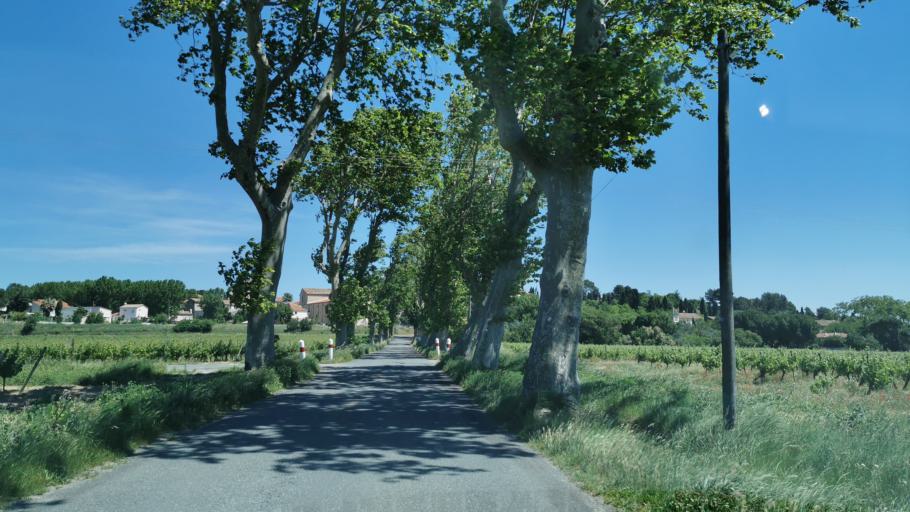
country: FR
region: Languedoc-Roussillon
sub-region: Departement de l'Aude
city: Canet
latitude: 43.2451
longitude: 2.8571
